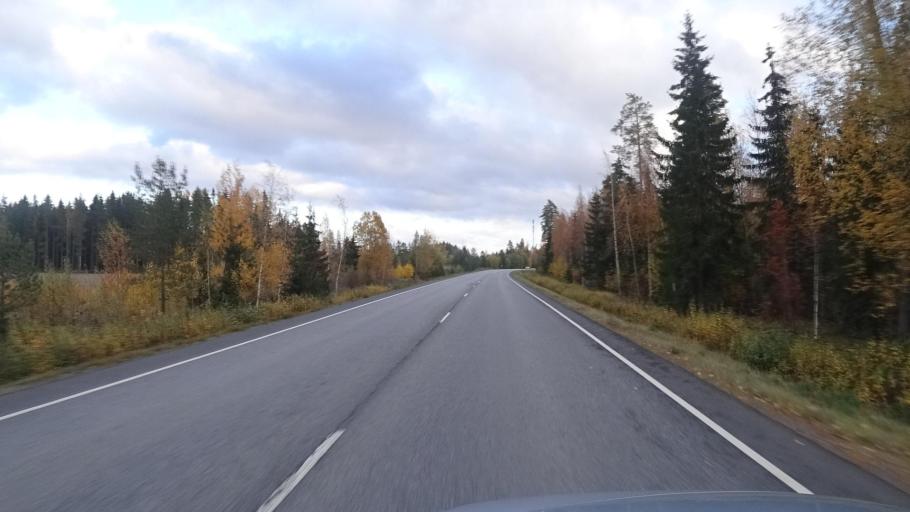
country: FI
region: Varsinais-Suomi
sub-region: Loimaa
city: Loimaa
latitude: 60.8806
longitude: 22.9847
